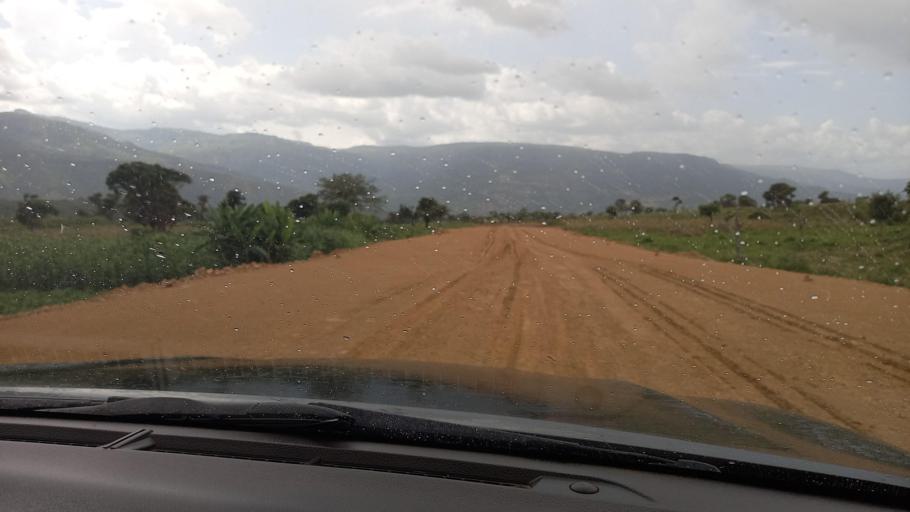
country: ET
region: Southern Nations, Nationalities, and People's Region
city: Mizan Teferi
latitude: 6.1754
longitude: 35.7061
